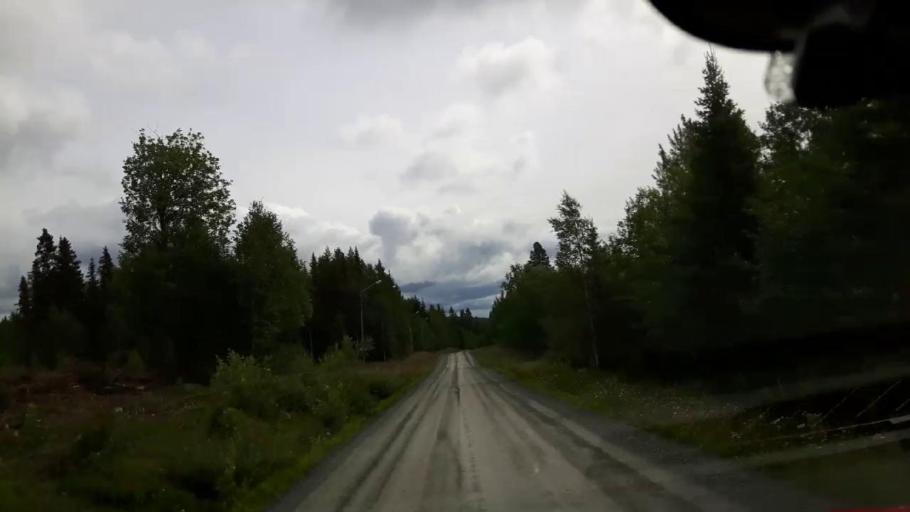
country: SE
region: Jaemtland
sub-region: Krokoms Kommun
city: Valla
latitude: 63.6696
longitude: 13.9579
